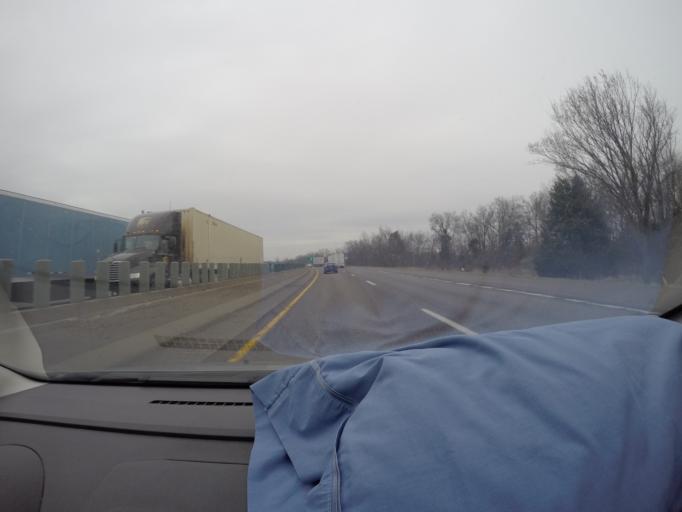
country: US
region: Missouri
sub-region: Saint Charles County
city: Wentzville
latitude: 38.8077
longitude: -90.8630
